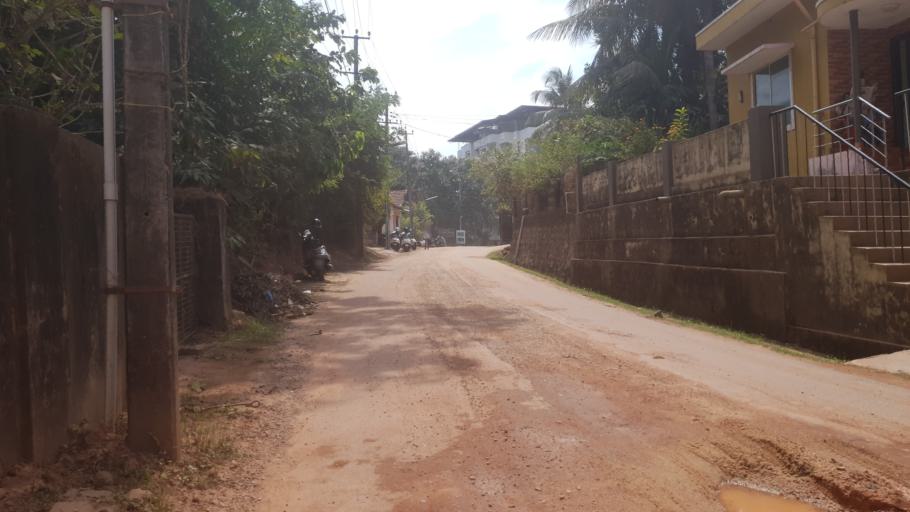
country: IN
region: Karnataka
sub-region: Dakshina Kannada
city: Ullal
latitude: 12.8448
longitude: 74.8471
